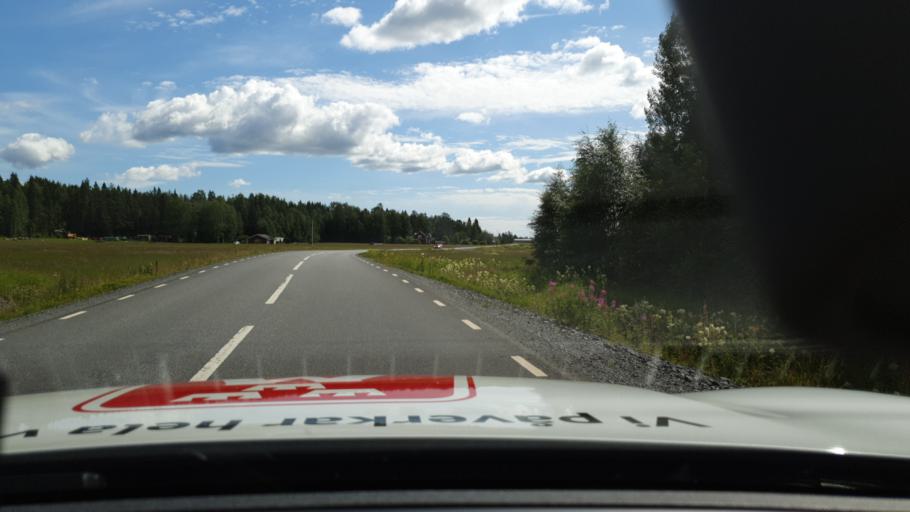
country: SE
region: Norrbotten
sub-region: Lulea Kommun
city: Sodra Sunderbyn
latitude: 65.8188
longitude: 21.9976
